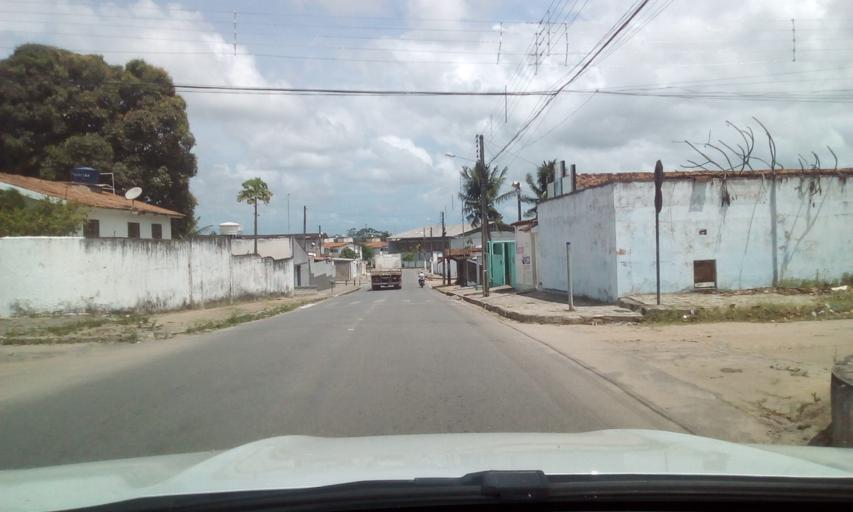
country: BR
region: Paraiba
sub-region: Bayeux
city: Bayeux
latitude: -7.1772
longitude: -34.9153
